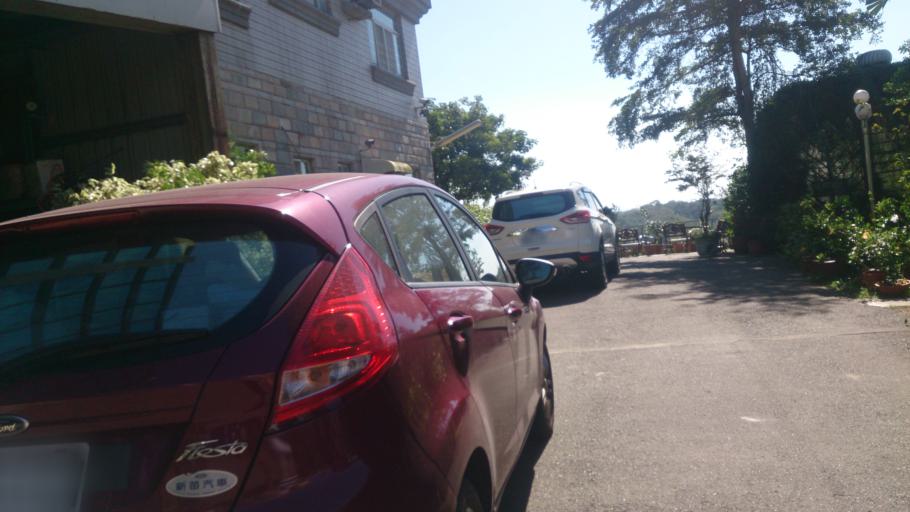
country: TW
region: Taiwan
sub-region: Hsinchu
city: Hsinchu
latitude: 24.7533
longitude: 120.9521
